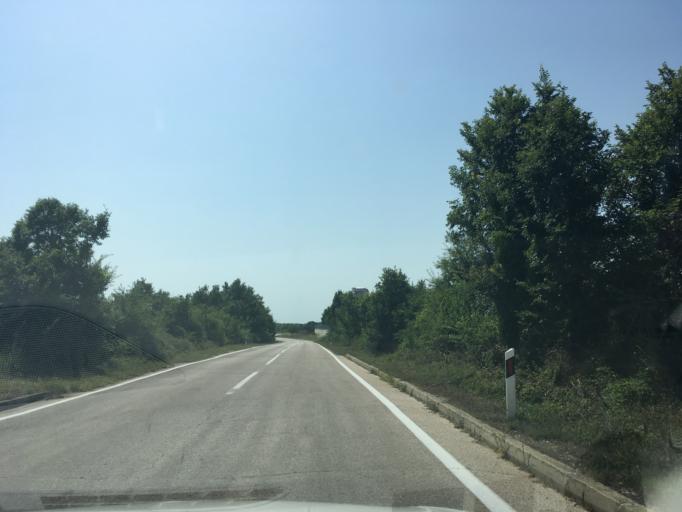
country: HR
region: Zadarska
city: Benkovac
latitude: 44.0226
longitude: 15.6257
